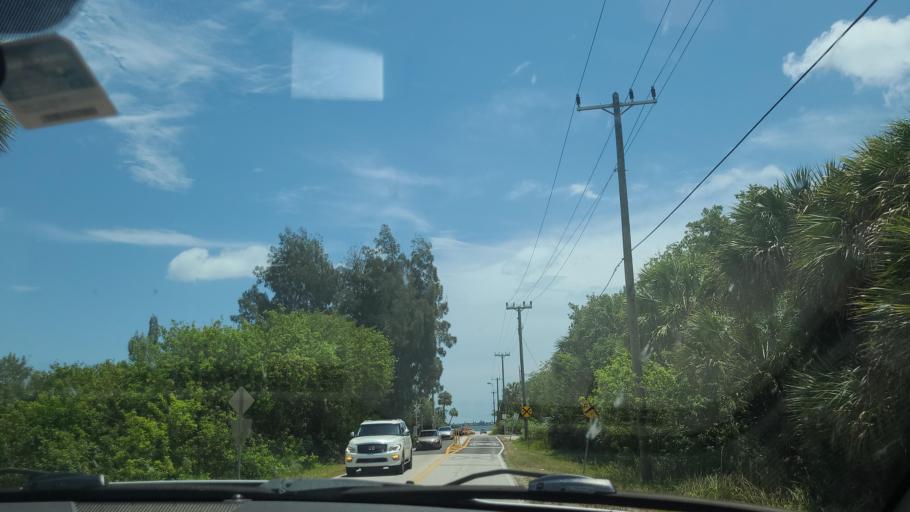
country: US
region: Florida
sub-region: Brevard County
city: Grant-Valkaria
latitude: 27.9638
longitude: -80.5448
